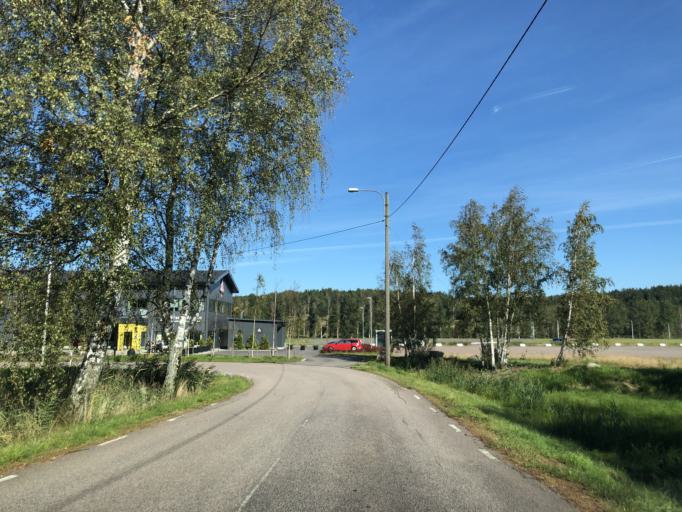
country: SE
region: Vaestra Goetaland
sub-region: Goteborg
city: Majorna
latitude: 57.7758
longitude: 11.9117
